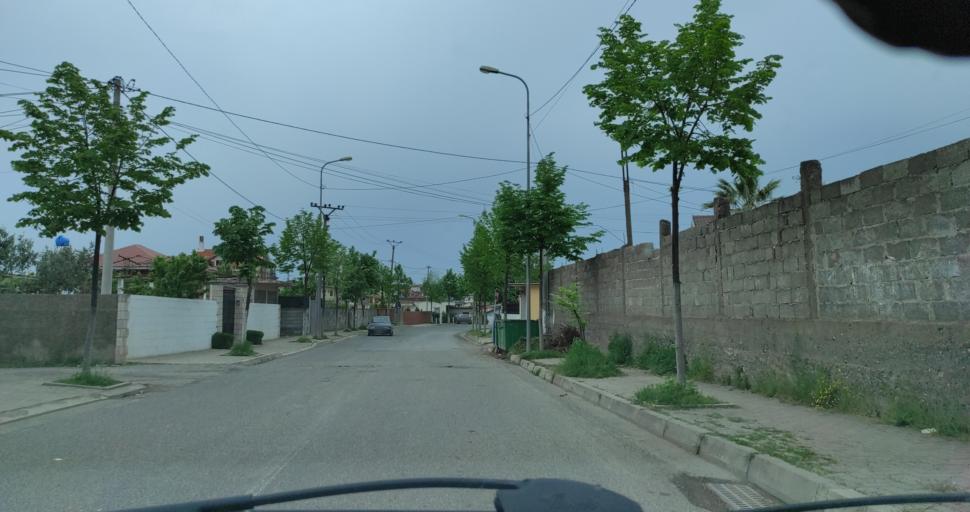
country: AL
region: Lezhe
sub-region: Rrethi i Kurbinit
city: Mamurras
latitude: 41.5812
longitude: 19.6919
